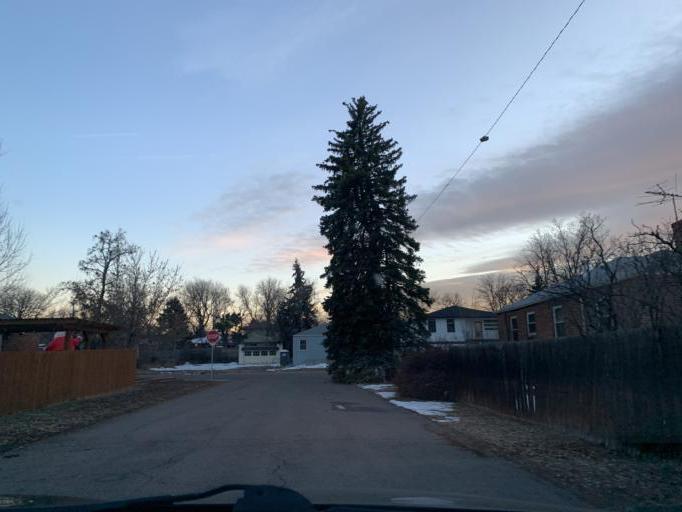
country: US
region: Colorado
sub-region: Adams County
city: Berkley
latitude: 39.7815
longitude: -105.0358
